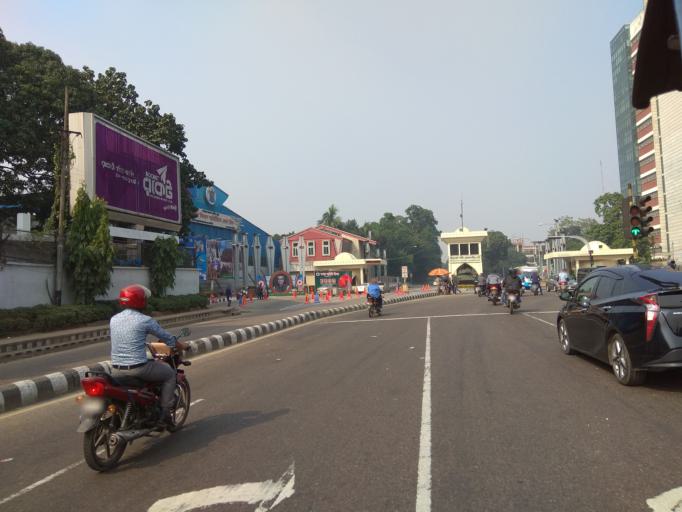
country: BD
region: Dhaka
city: Azimpur
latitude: 23.7749
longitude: 90.3899
